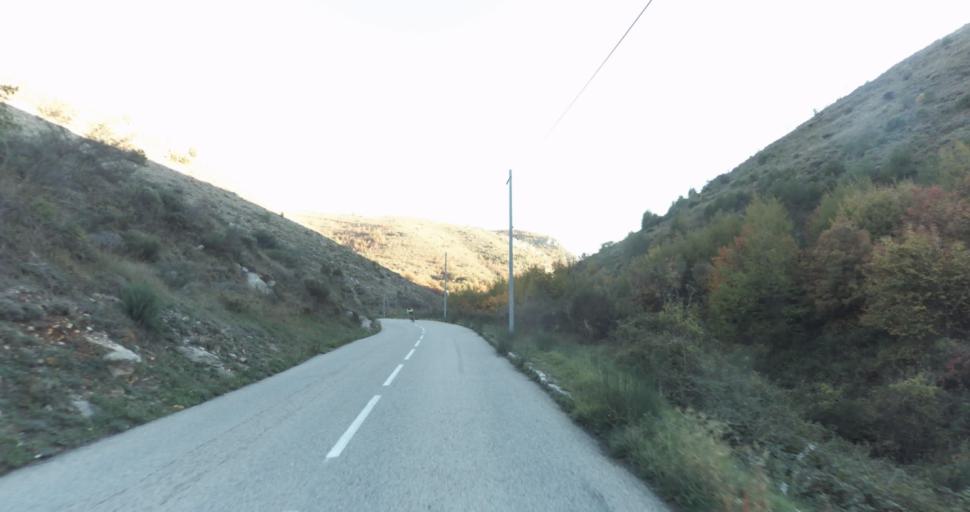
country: FR
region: Provence-Alpes-Cote d'Azur
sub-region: Departement des Alpes-Maritimes
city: Vence
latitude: 43.7445
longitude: 7.1028
